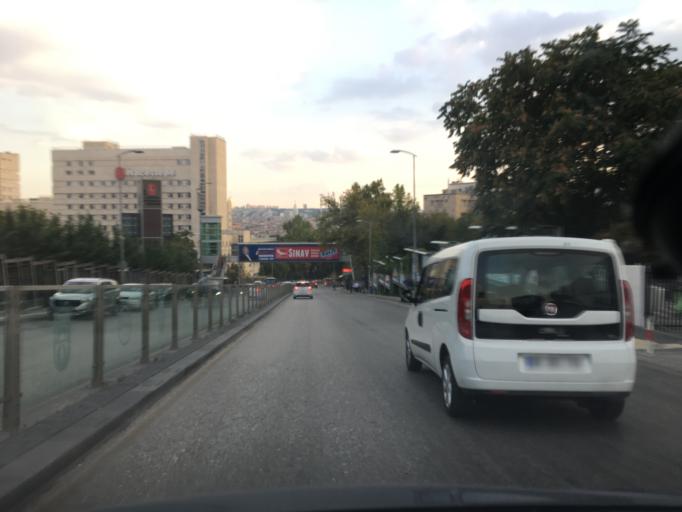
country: TR
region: Ankara
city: Ankara
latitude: 39.9322
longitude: 32.8599
